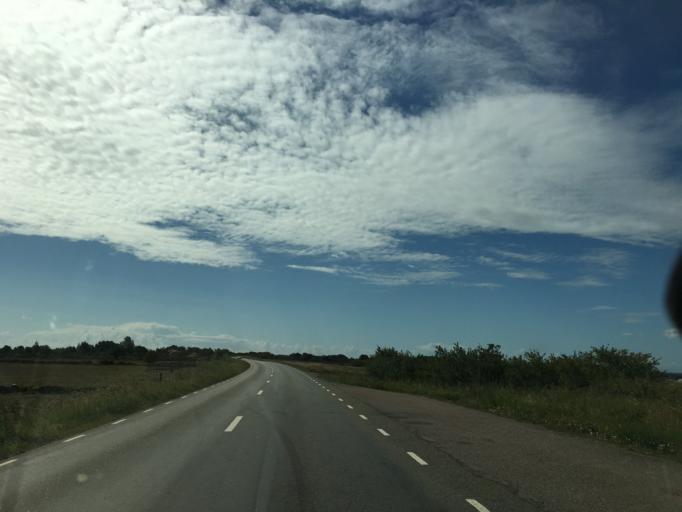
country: SE
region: Kalmar
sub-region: Morbylanga Kommun
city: Moerbylanga
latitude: 56.4902
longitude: 16.4262
